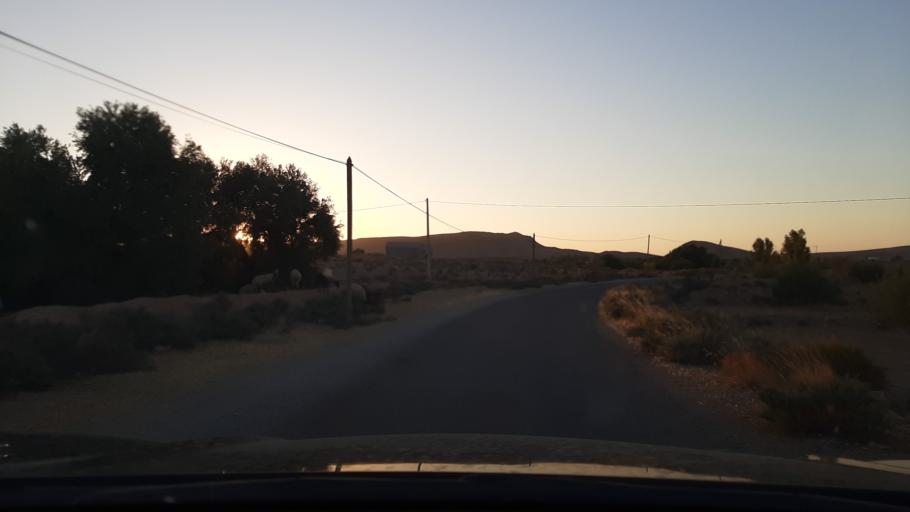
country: TN
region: Qabis
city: Matmata
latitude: 33.5617
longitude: 10.1817
